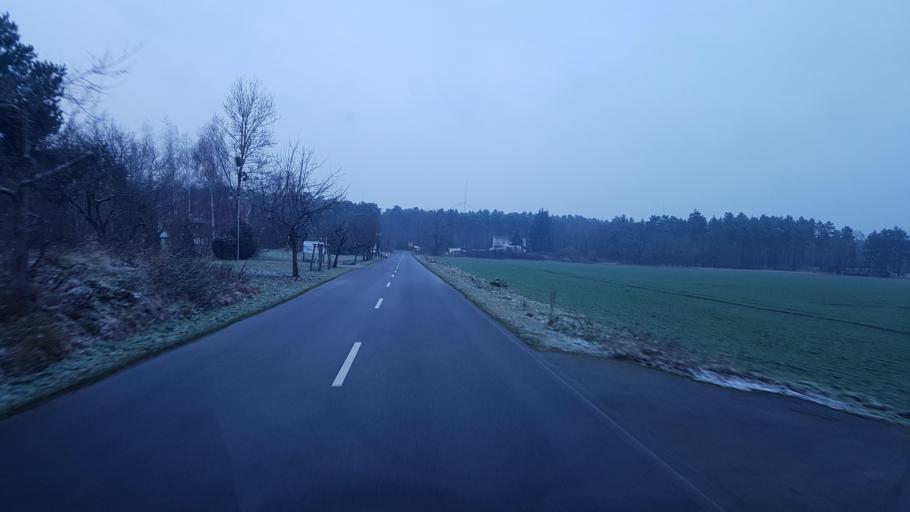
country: DE
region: Brandenburg
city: Kasel-Golzig
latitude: 51.9474
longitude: 13.7874
